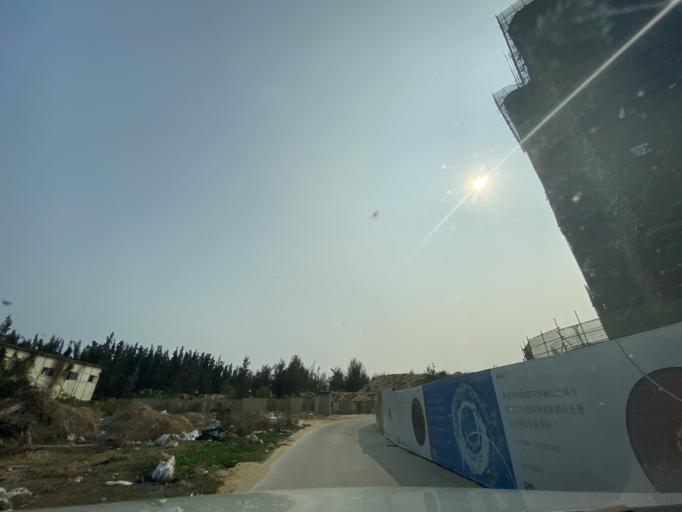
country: CN
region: Hainan
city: Yingzhou
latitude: 18.3934
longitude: 109.8553
